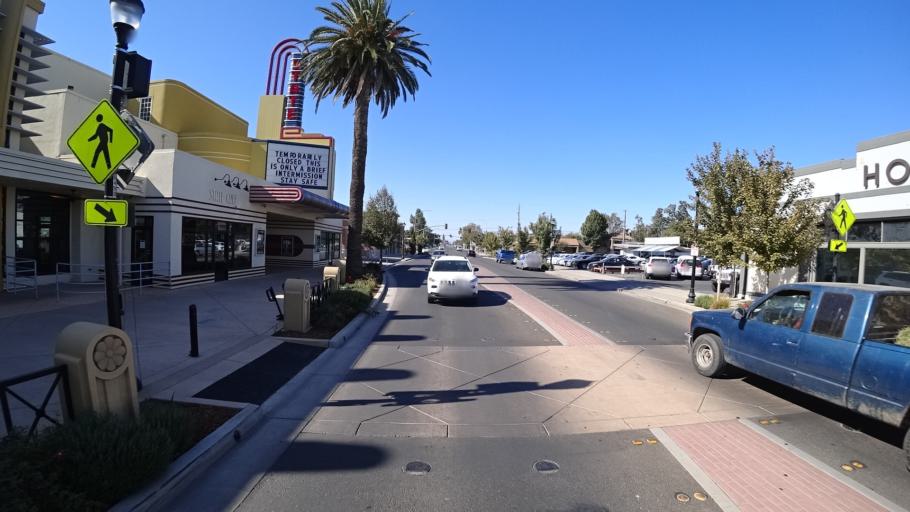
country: US
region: California
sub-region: Yolo County
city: Woodland
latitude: 38.6775
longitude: -121.7772
